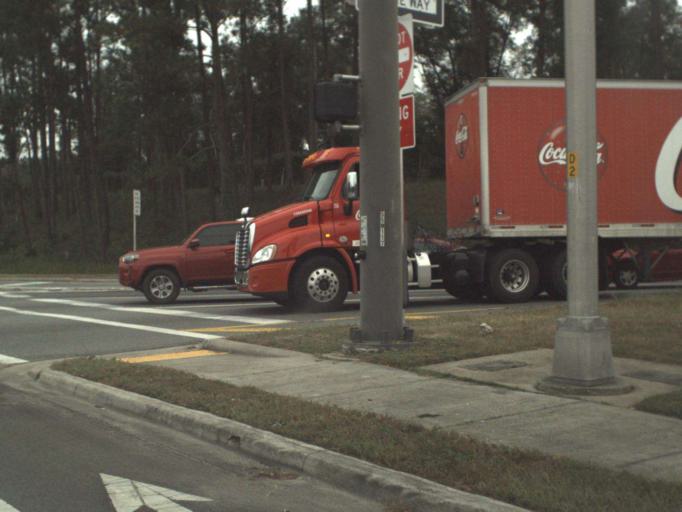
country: US
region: Florida
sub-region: Leon County
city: Tallahassee
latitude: 30.4804
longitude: -84.3630
